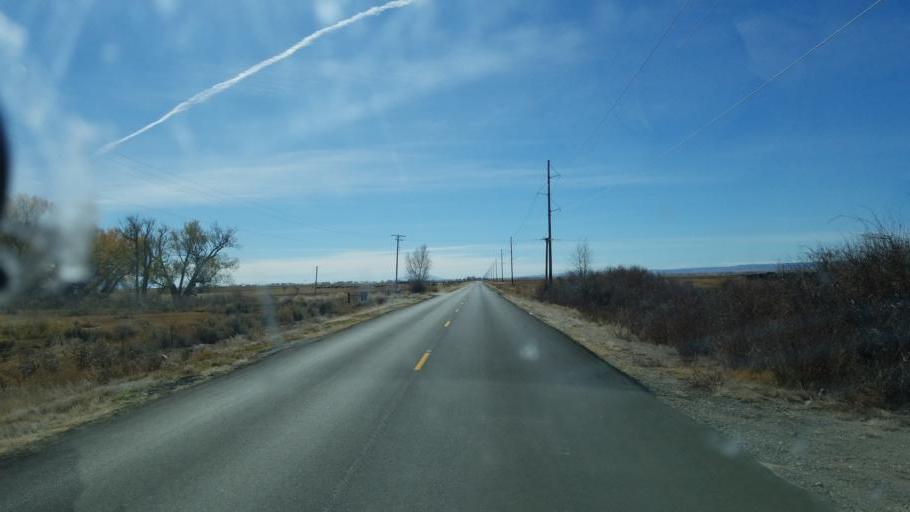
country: US
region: Colorado
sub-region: Rio Grande County
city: Monte Vista
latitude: 37.5253
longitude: -106.0942
